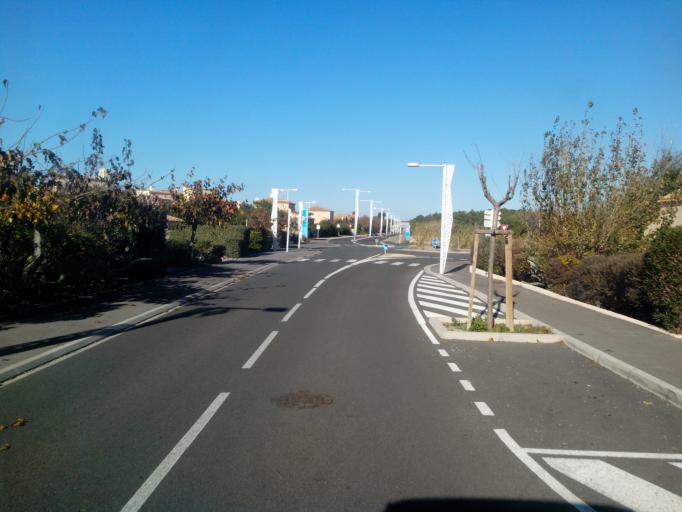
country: FR
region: Languedoc-Roussillon
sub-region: Departement des Pyrenees-Orientales
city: Le Barcares
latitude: 42.8406
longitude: 3.0366
